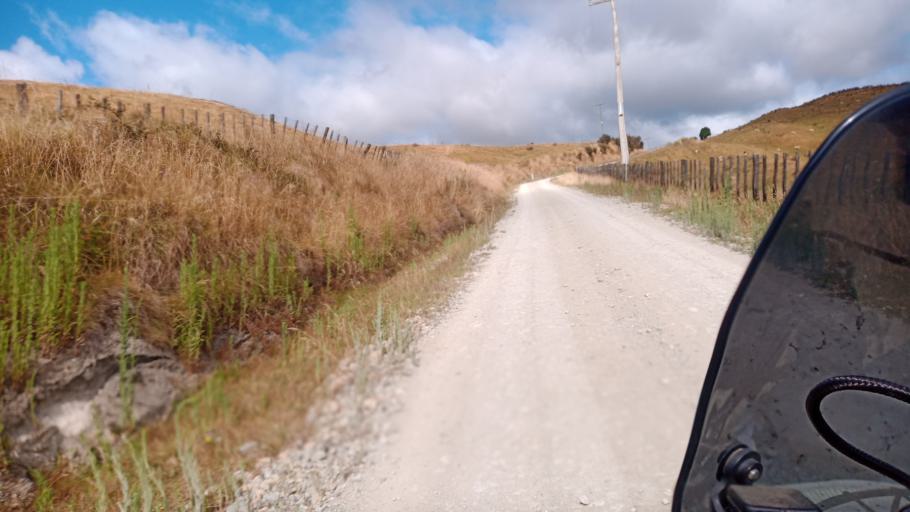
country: NZ
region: Hawke's Bay
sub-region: Wairoa District
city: Wairoa
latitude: -38.6036
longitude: 177.4751
